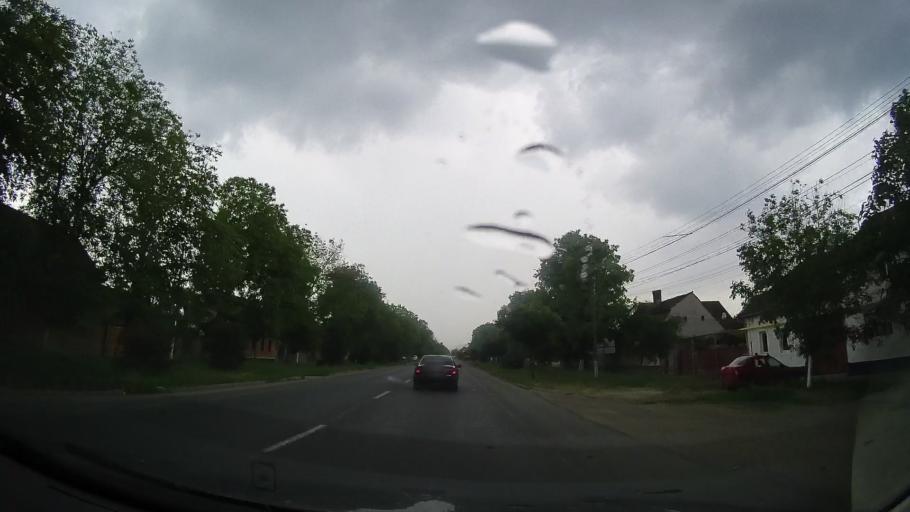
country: RO
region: Caras-Severin
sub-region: Municipiul Caransebes
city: Caransebes
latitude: 45.3976
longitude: 22.2255
